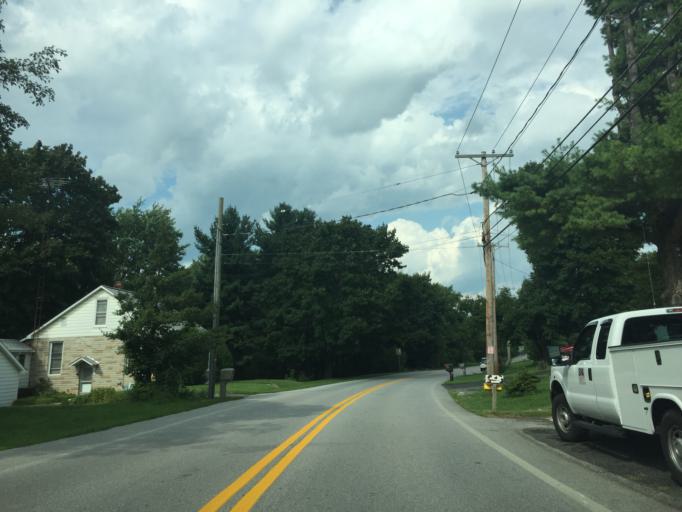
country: US
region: Maryland
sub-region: Carroll County
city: Westminster
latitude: 39.5909
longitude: -76.9937
